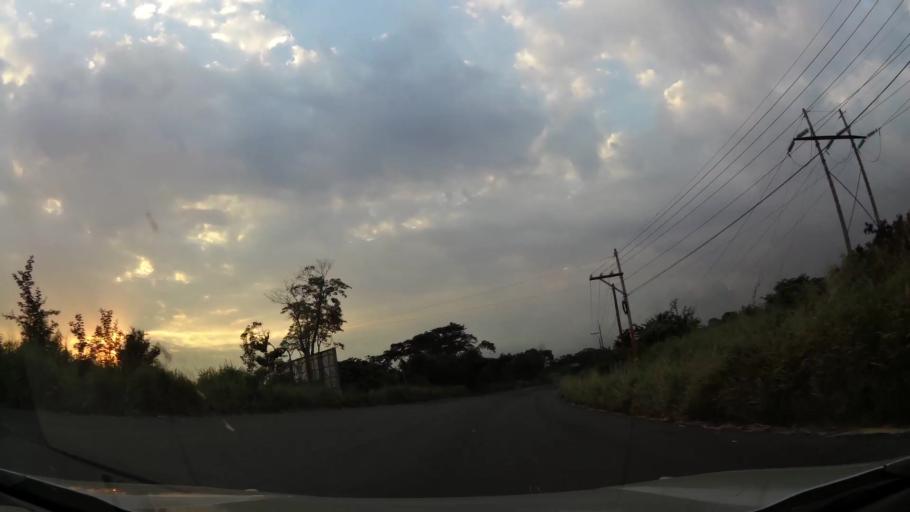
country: GT
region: Escuintla
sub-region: Municipio de La Democracia
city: La Democracia
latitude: 14.2767
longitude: -90.9189
